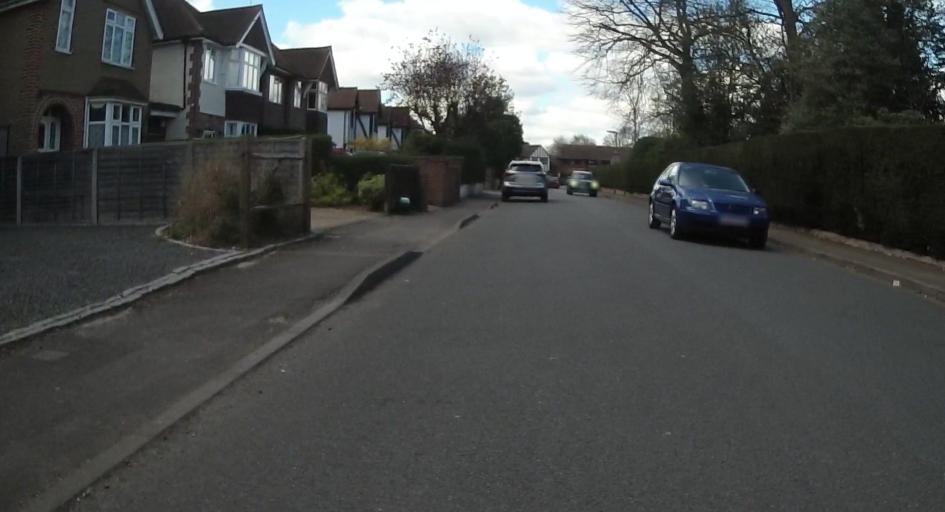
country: GB
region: England
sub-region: Surrey
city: Addlestone
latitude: 51.3722
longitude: -0.5014
